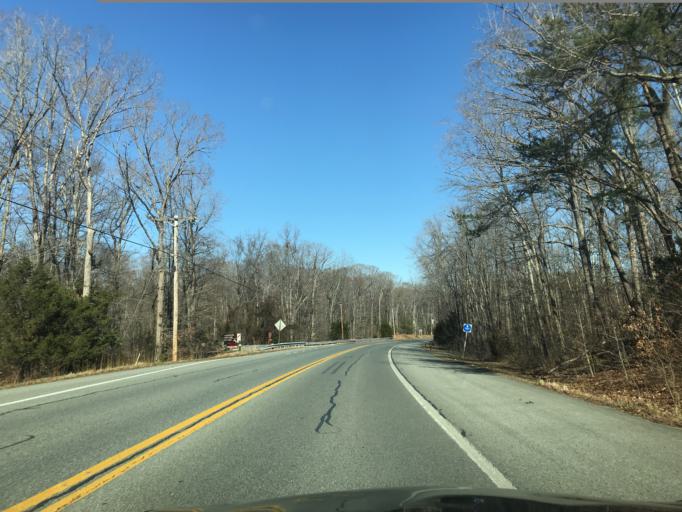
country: US
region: Maryland
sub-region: Charles County
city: Indian Head
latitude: 38.5539
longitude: -77.1743
